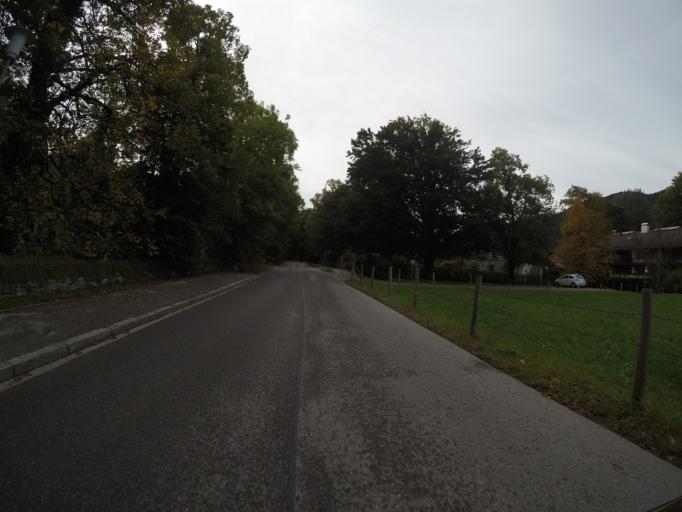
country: DE
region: Bavaria
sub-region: Upper Bavaria
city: Rottach-Egern
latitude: 47.6908
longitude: 11.7603
